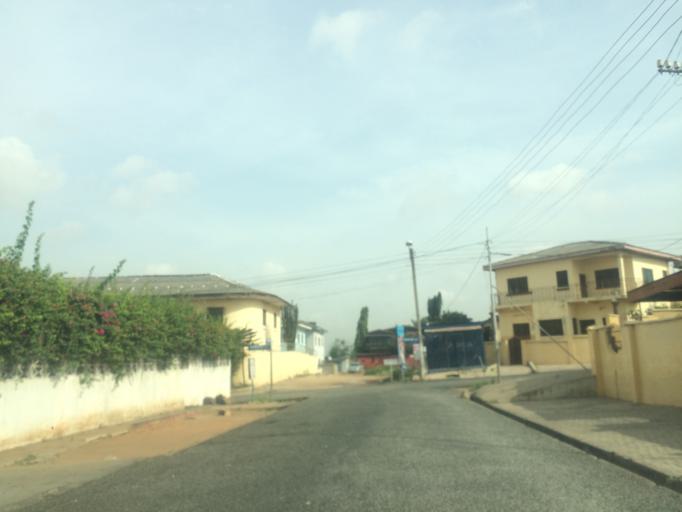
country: GH
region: Greater Accra
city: Accra
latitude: 5.5647
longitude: -0.2106
